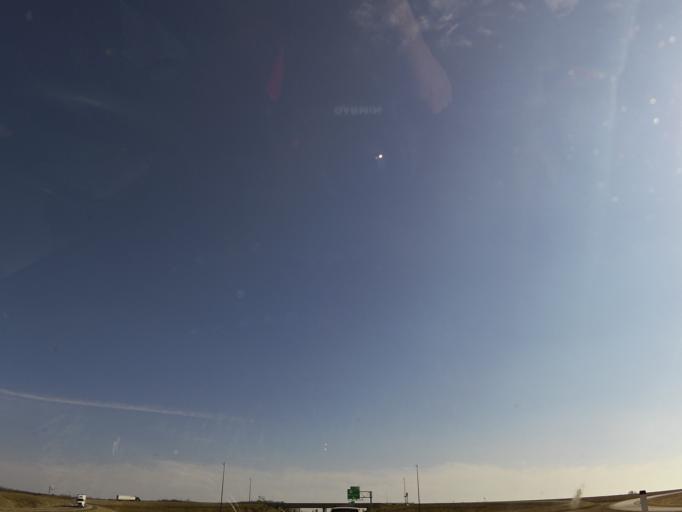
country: US
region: Minnesota
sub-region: Steele County
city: Owatonna
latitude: 44.0633
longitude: -93.2512
